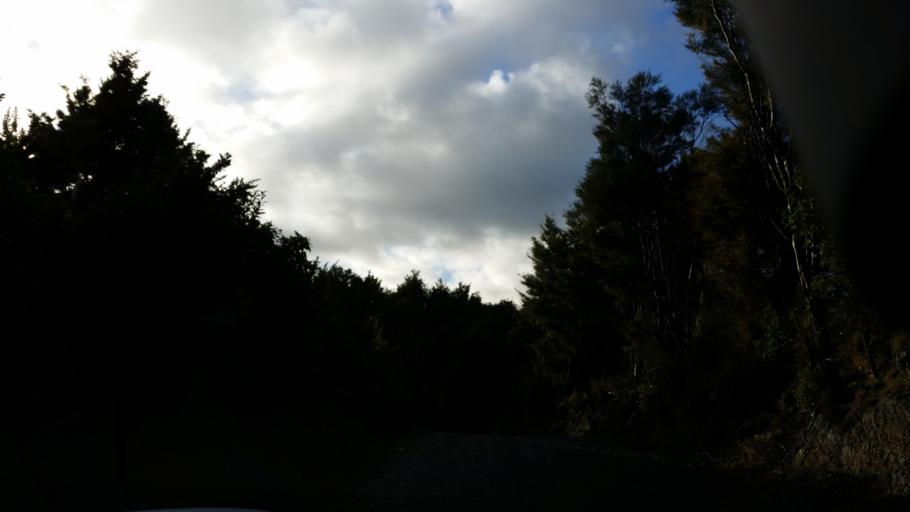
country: NZ
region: Northland
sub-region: Whangarei
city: Maungatapere
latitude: -35.7793
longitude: 174.0940
